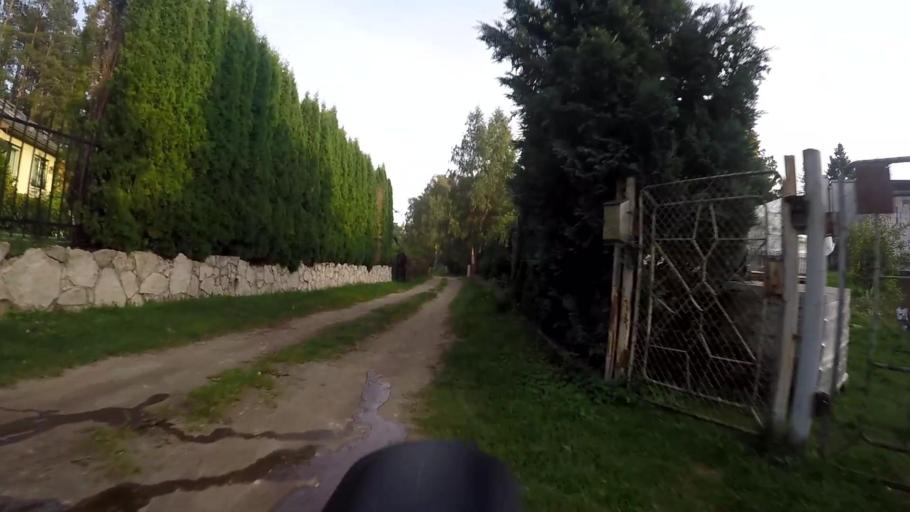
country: LV
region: Saulkrastu
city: Saulkrasti
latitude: 57.1890
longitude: 24.3539
